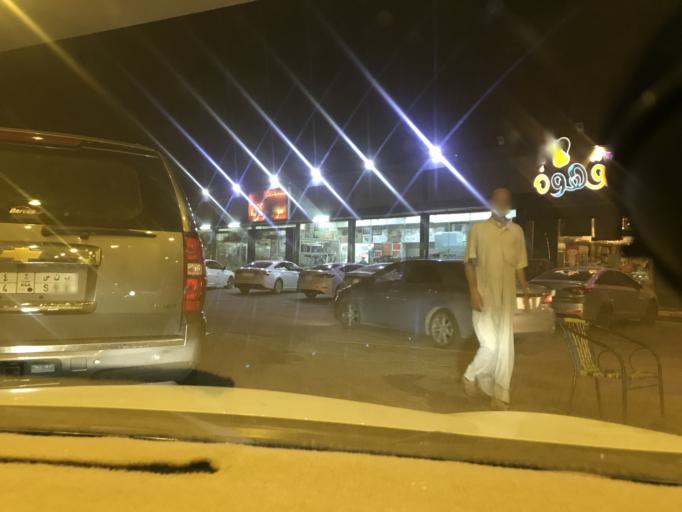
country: SA
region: Ar Riyad
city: Riyadh
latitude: 24.8505
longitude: 46.6028
